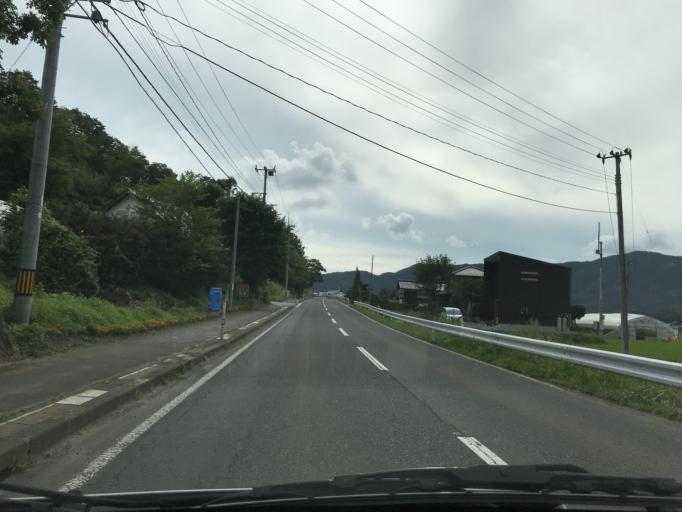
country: JP
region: Iwate
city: Tono
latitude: 39.3511
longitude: 141.5529
